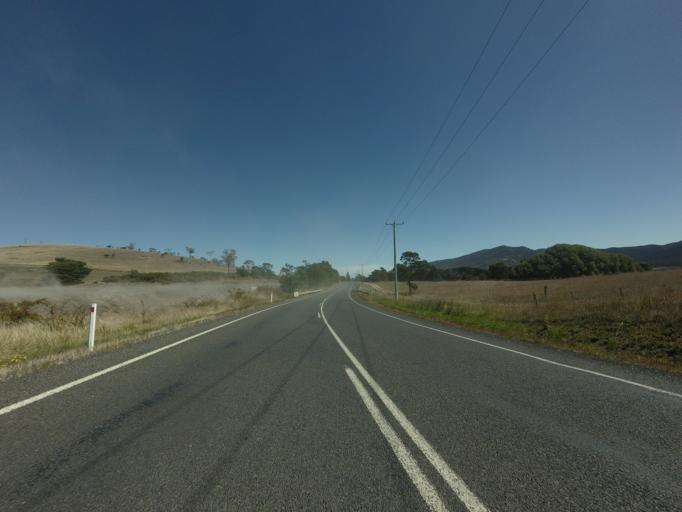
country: AU
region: Tasmania
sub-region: Break O'Day
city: St Helens
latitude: -41.7196
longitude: 147.8320
